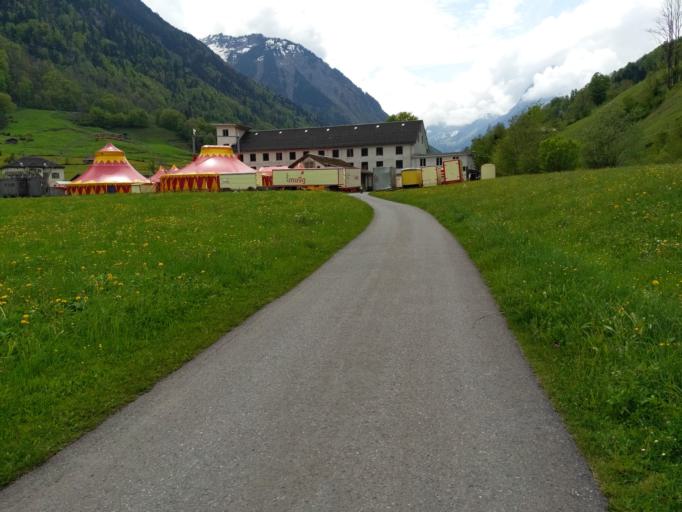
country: CH
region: Glarus
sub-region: Glarus
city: Luchsingen
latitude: 46.9470
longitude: 9.0236
